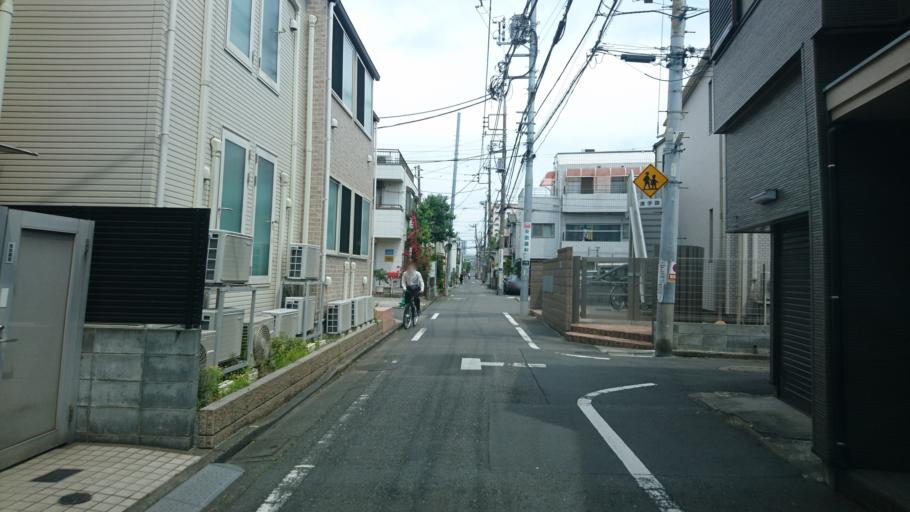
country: JP
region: Kanagawa
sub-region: Kawasaki-shi
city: Kawasaki
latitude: 35.5724
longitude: 139.7281
